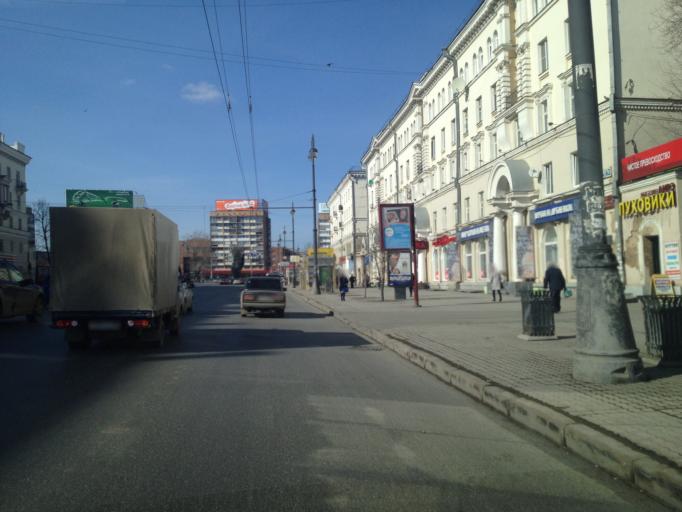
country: RU
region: Sverdlovsk
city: Yekaterinburg
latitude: 56.8541
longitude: 60.6046
